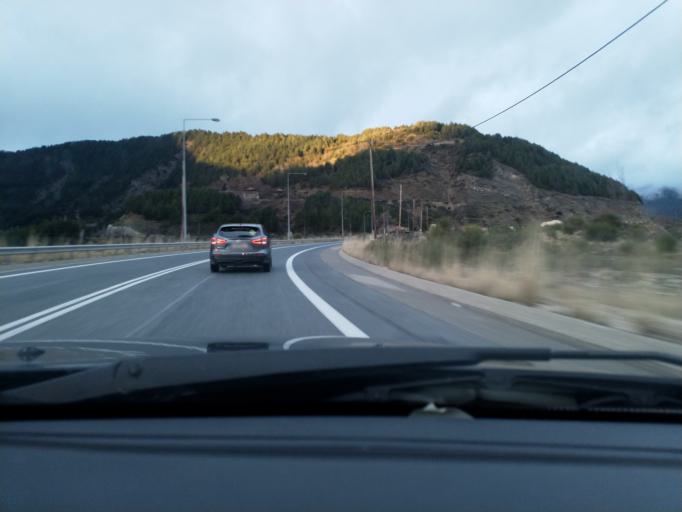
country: GR
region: Epirus
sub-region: Nomos Ioanninon
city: Metsovo
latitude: 39.7616
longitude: 21.1728
